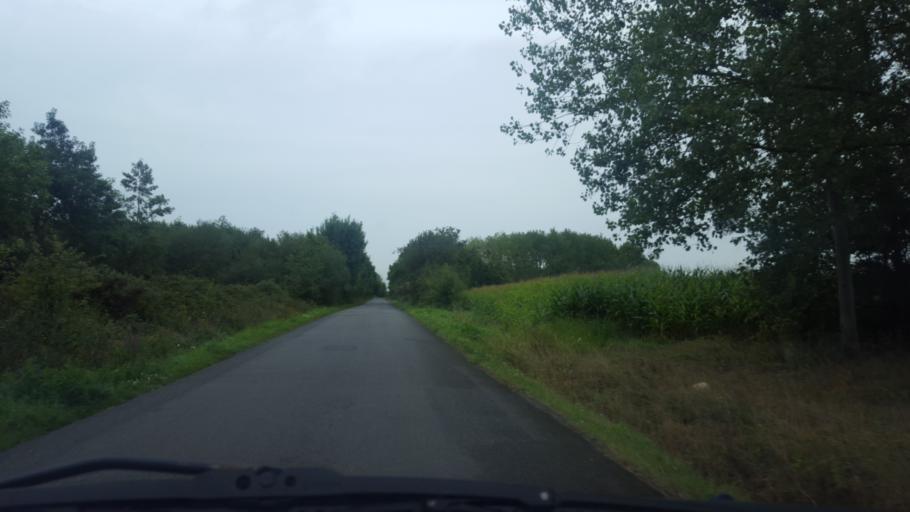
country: FR
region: Pays de la Loire
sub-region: Departement de la Loire-Atlantique
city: Saint-Philbert-de-Grand-Lieu
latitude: 47.0417
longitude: -1.6645
